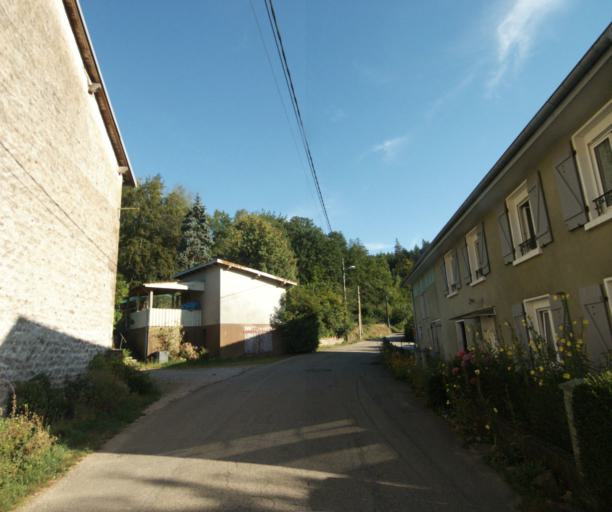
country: FR
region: Lorraine
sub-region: Departement des Vosges
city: Chantraine
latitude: 48.1446
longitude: 6.4403
